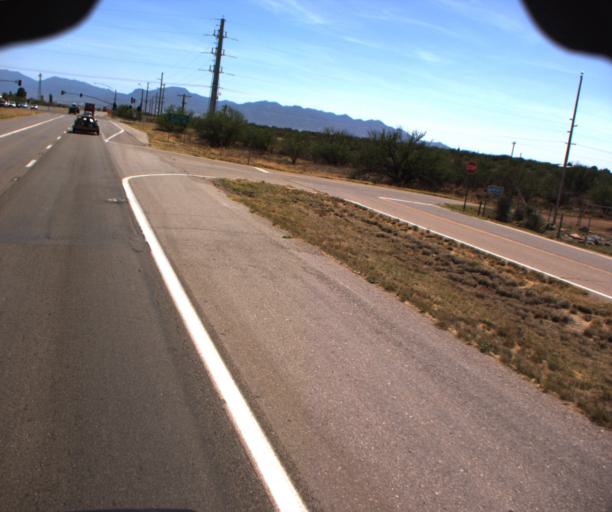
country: US
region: Arizona
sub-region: Cochise County
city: Huachuca City
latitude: 31.6945
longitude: -110.3504
